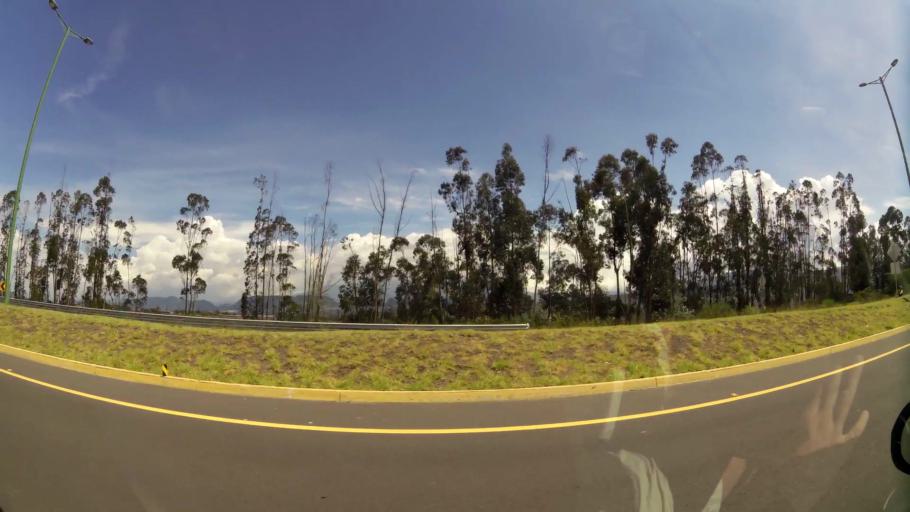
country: EC
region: Pichincha
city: Quito
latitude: -0.1342
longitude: -78.3595
